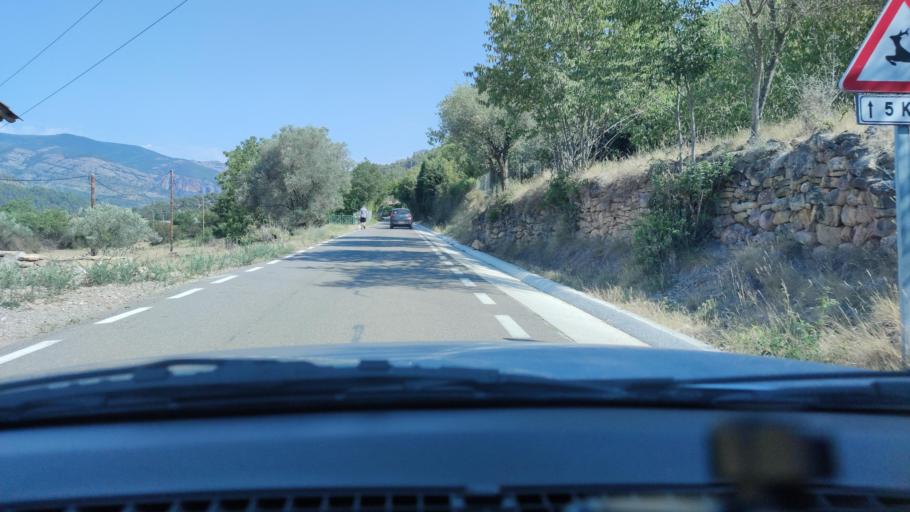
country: ES
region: Catalonia
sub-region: Provincia de Lleida
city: Senterada
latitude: 42.2548
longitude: 0.9642
